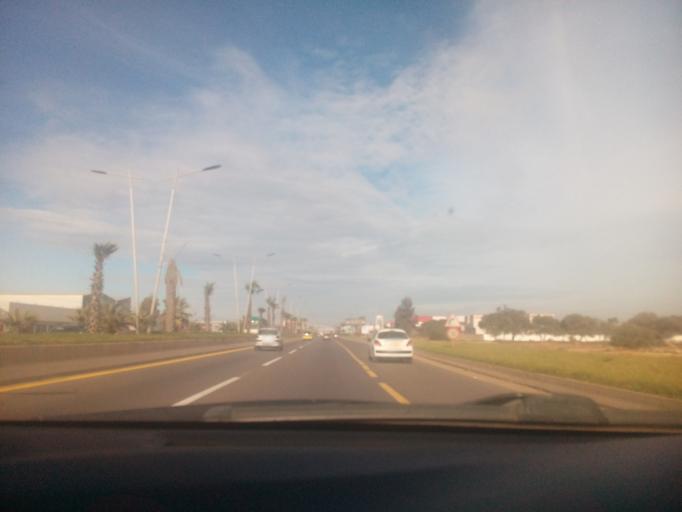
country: DZ
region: Oran
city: Es Senia
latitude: 35.6341
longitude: -0.5876
